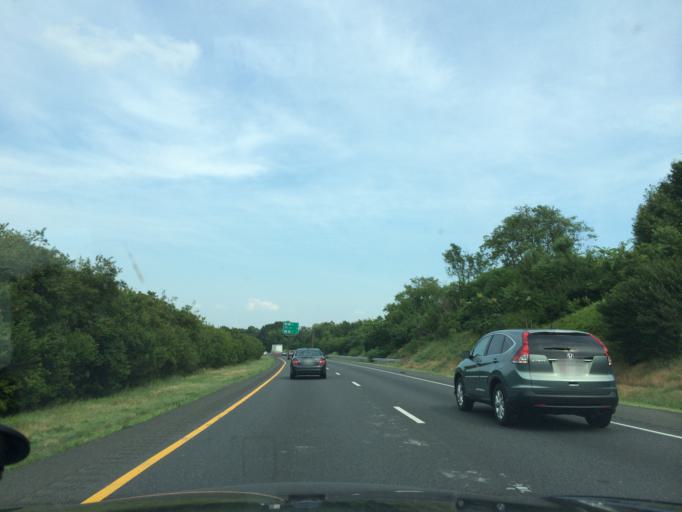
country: US
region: Maryland
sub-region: Frederick County
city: Braddock Heights
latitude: 39.4050
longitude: -77.4658
